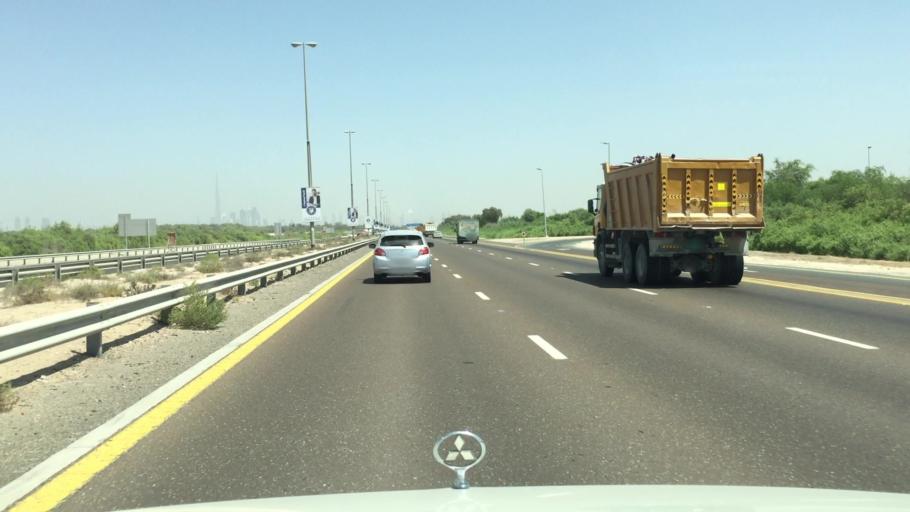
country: AE
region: Dubai
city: Dubai
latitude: 25.1334
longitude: 55.3536
